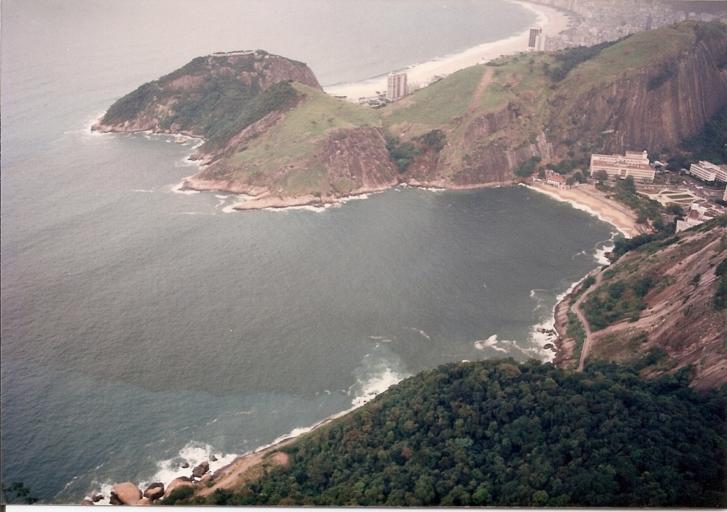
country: BR
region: Rio de Janeiro
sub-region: Rio De Janeiro
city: Rio de Janeiro
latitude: -22.9530
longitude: -43.1663
